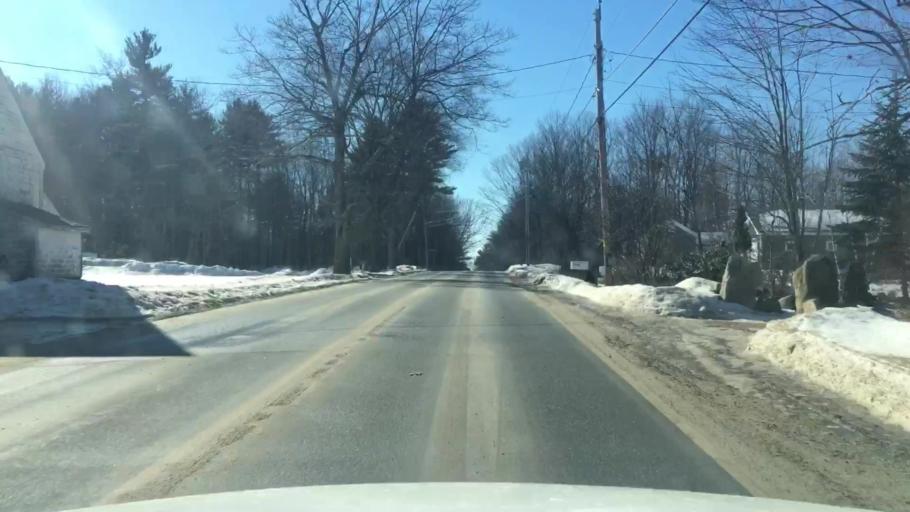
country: US
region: Maine
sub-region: Cumberland County
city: North Windham
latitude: 43.8537
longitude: -70.3481
